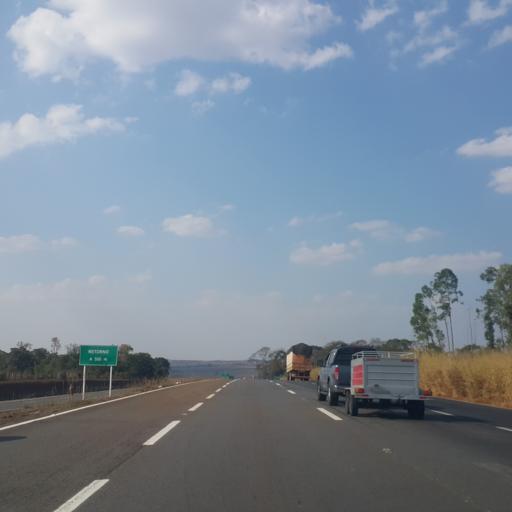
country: BR
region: Goias
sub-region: Abadiania
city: Abadiania
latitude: -16.2842
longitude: -48.7950
